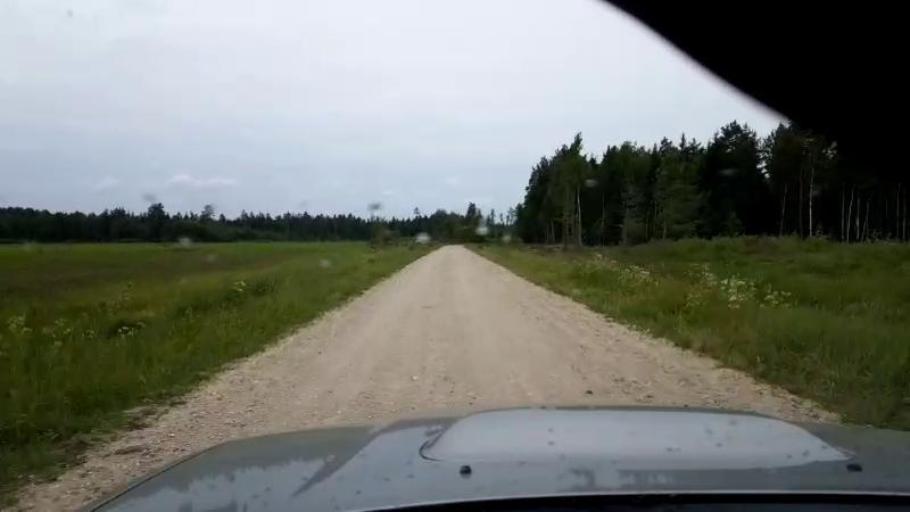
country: EE
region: Paernumaa
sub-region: Halinga vald
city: Parnu-Jaagupi
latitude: 58.5414
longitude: 24.5977
